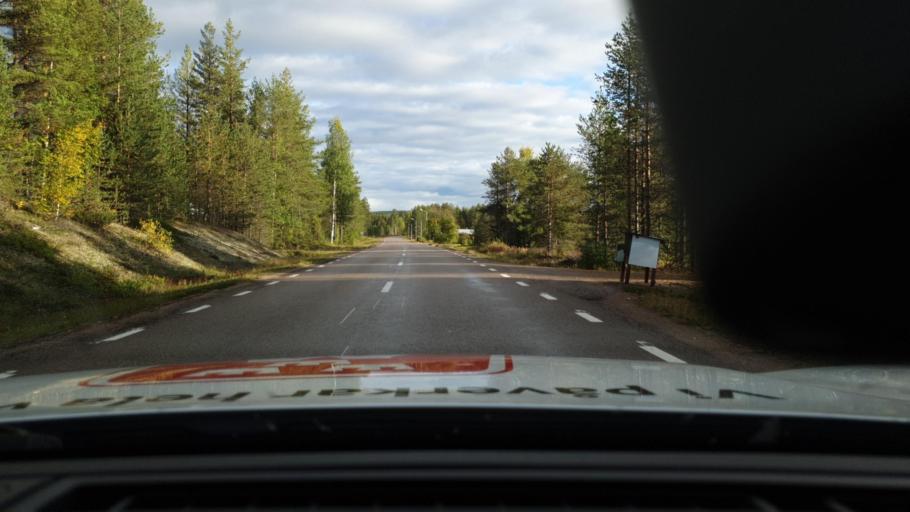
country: SE
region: Norrbotten
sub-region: Overkalix Kommun
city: OEverkalix
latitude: 66.6243
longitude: 22.7400
